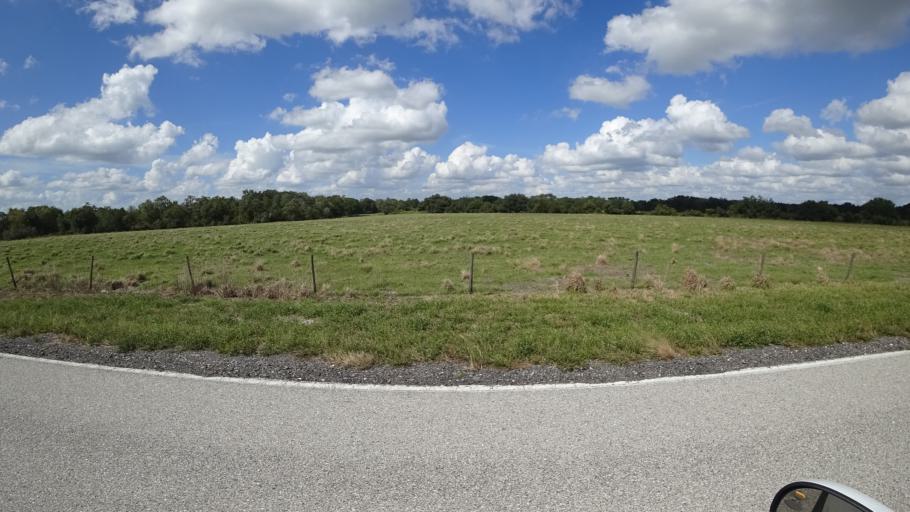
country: US
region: Florida
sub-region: Sarasota County
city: Lake Sarasota
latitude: 27.3226
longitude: -82.1685
